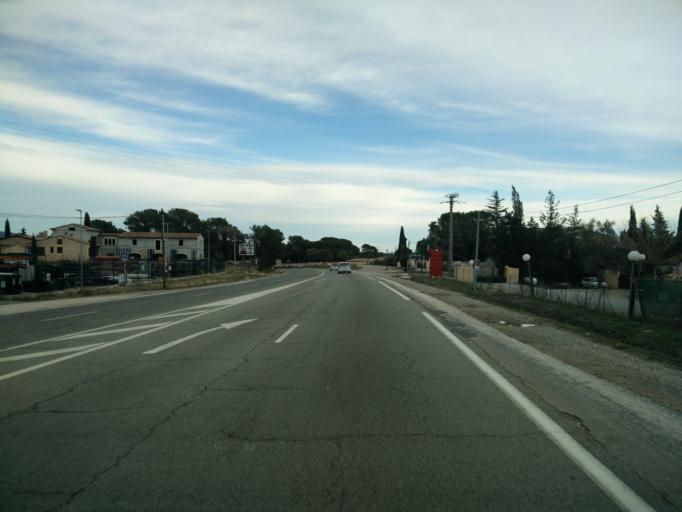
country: FR
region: Provence-Alpes-Cote d'Azur
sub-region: Departement du Var
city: Roquebrune-sur-Argens
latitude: 43.4630
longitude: 6.6260
